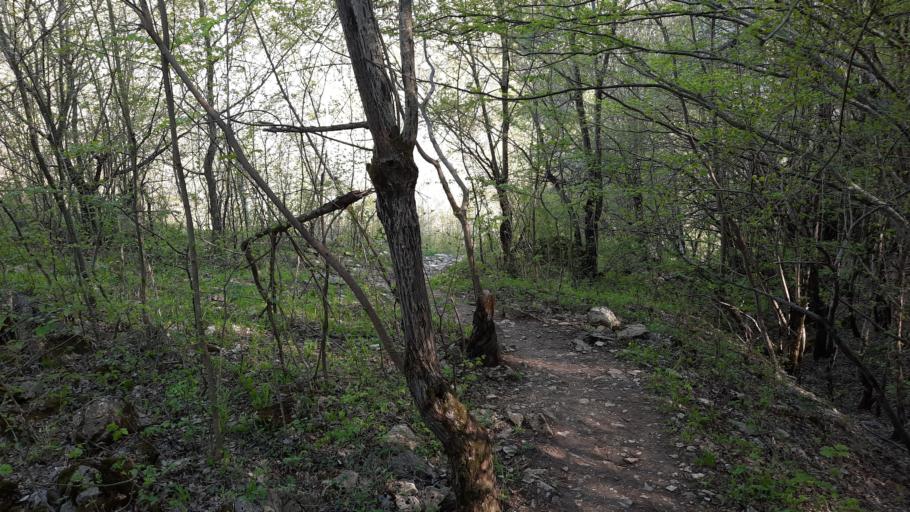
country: RU
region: Adygeya
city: Kamennomostskiy
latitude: 44.2787
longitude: 40.1891
